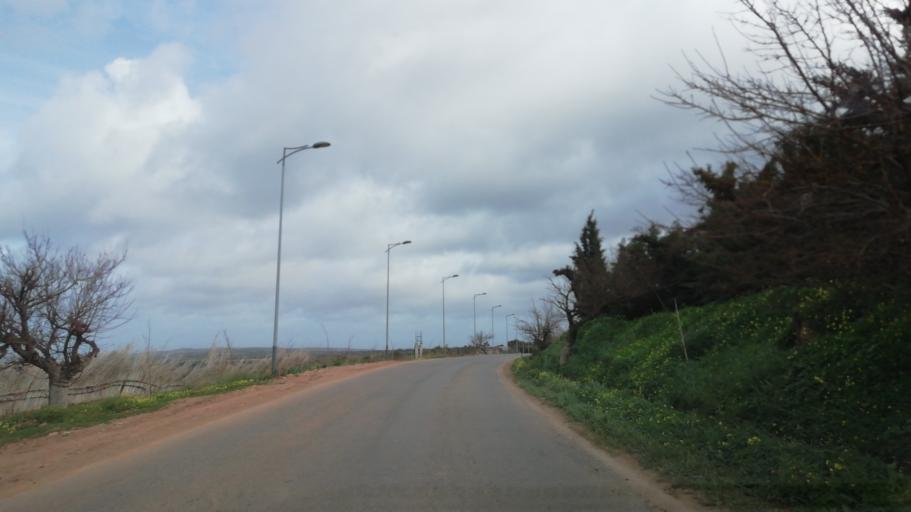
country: DZ
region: Oran
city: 'Ain el Turk
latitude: 35.6930
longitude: -0.8599
